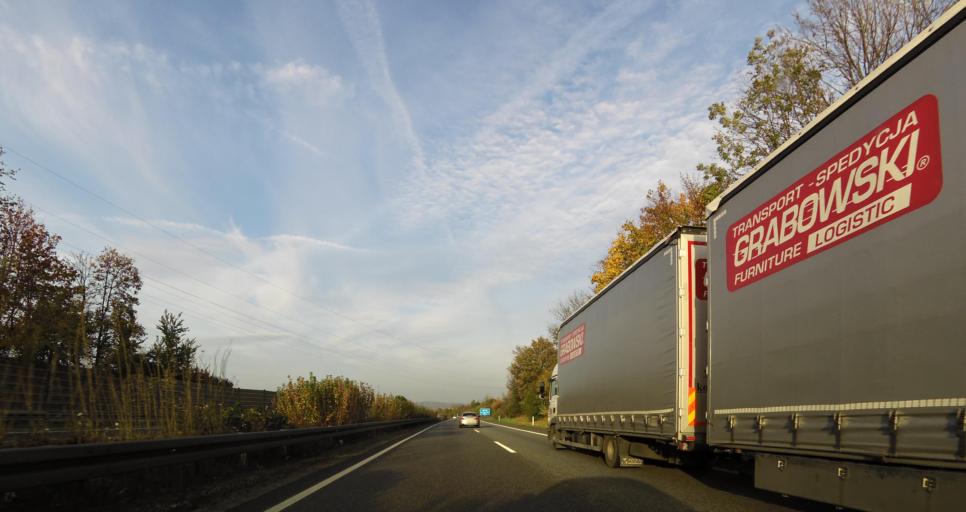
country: DE
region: Lower Saxony
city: Hillerse
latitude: 51.6892
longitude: 9.9305
